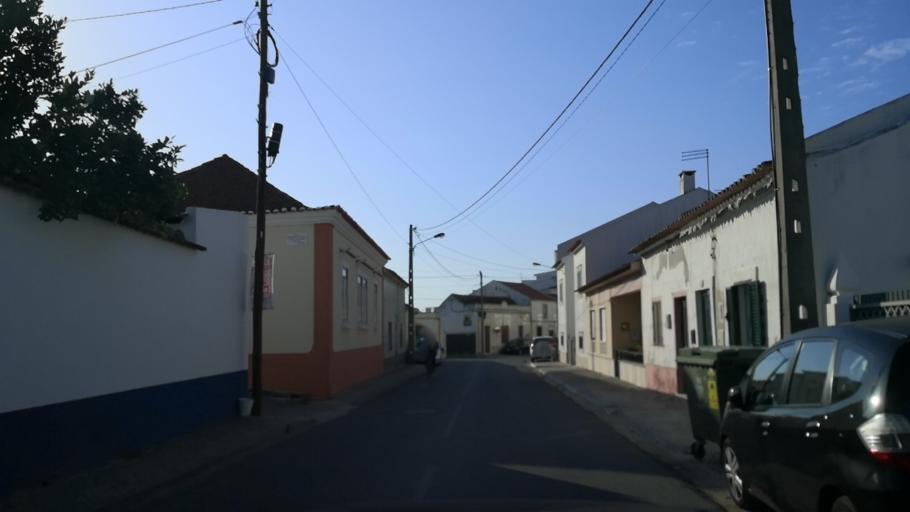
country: PT
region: Santarem
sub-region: Santarem
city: Santarem
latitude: 39.2949
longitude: -8.6573
